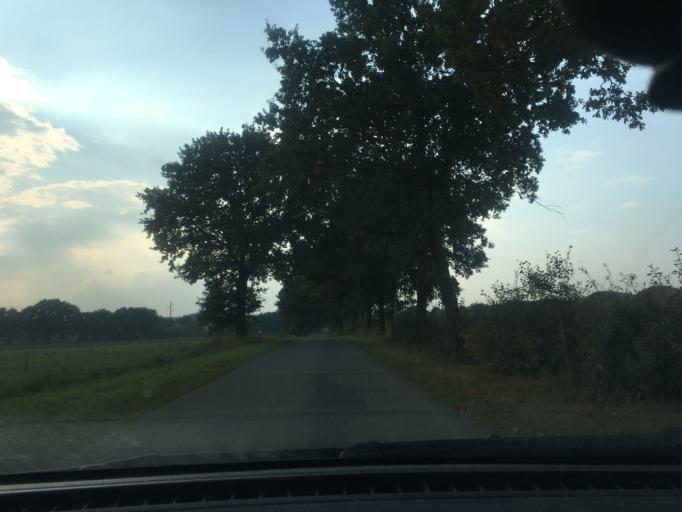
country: DE
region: Lower Saxony
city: Vastorf
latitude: 53.2039
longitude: 10.5665
